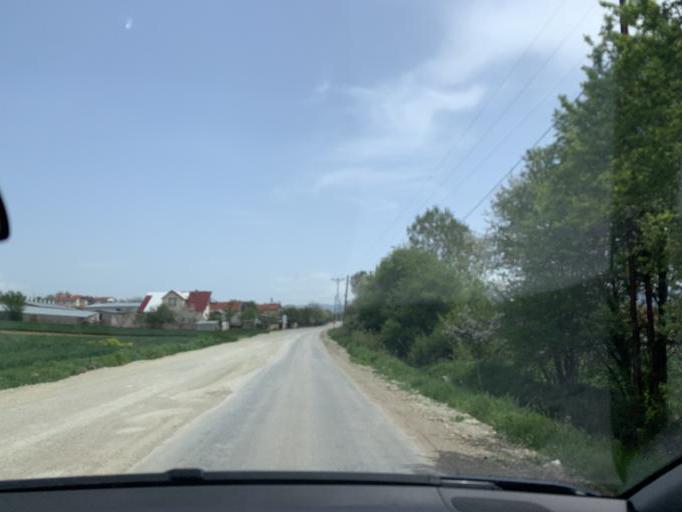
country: TR
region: Bolu
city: Bolu
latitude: 40.7620
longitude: 31.7040
